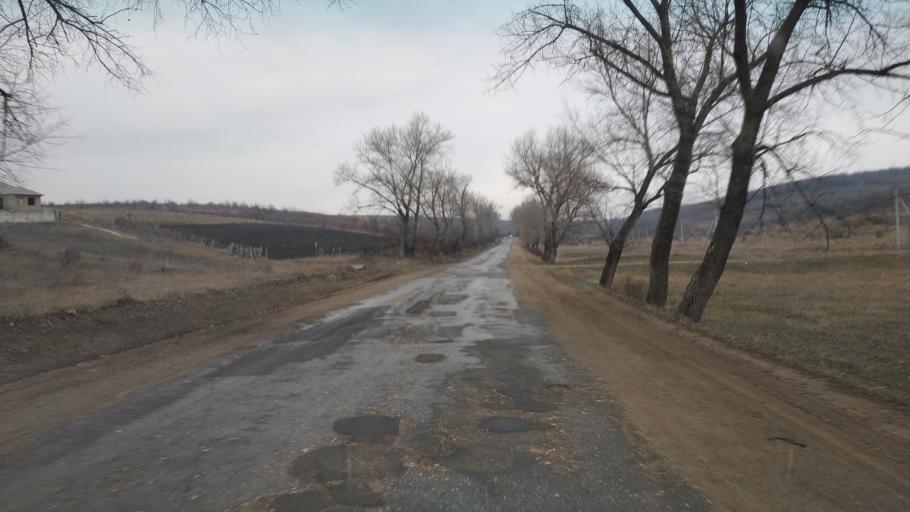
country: MD
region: Chisinau
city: Singera
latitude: 46.8421
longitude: 28.9804
